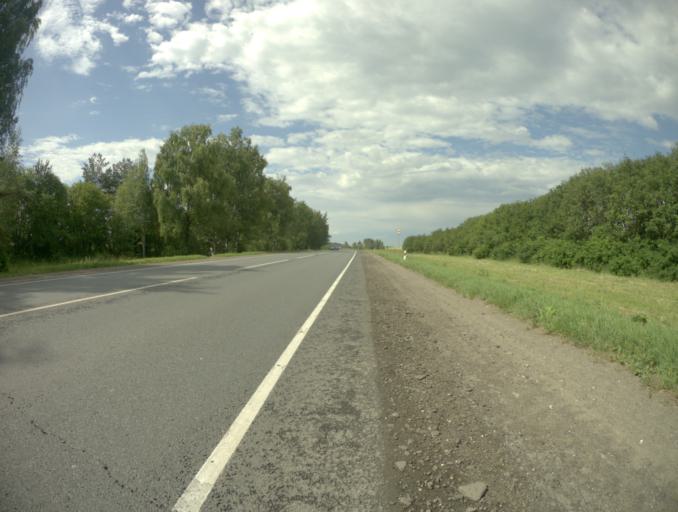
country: RU
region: Vladimir
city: Suzdal'
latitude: 56.3542
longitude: 40.4720
